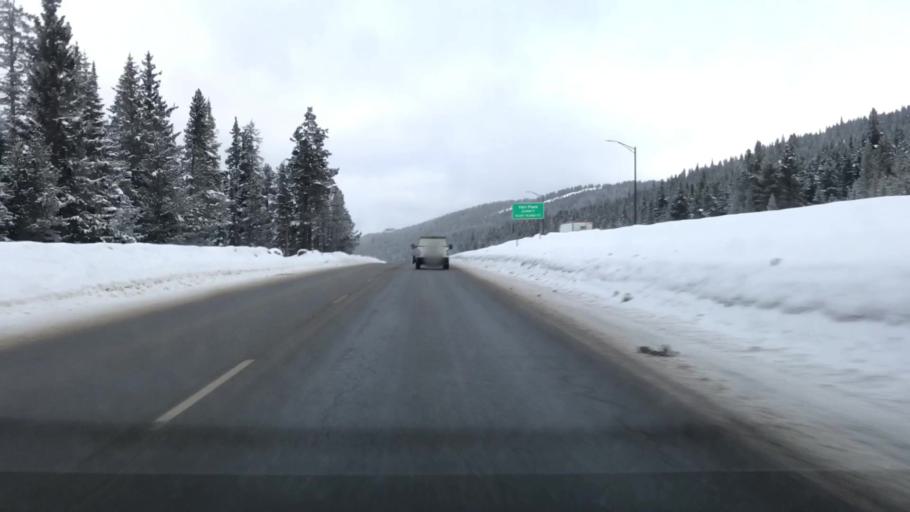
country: US
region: Colorado
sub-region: Summit County
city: Frisco
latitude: 39.5409
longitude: -106.2160
